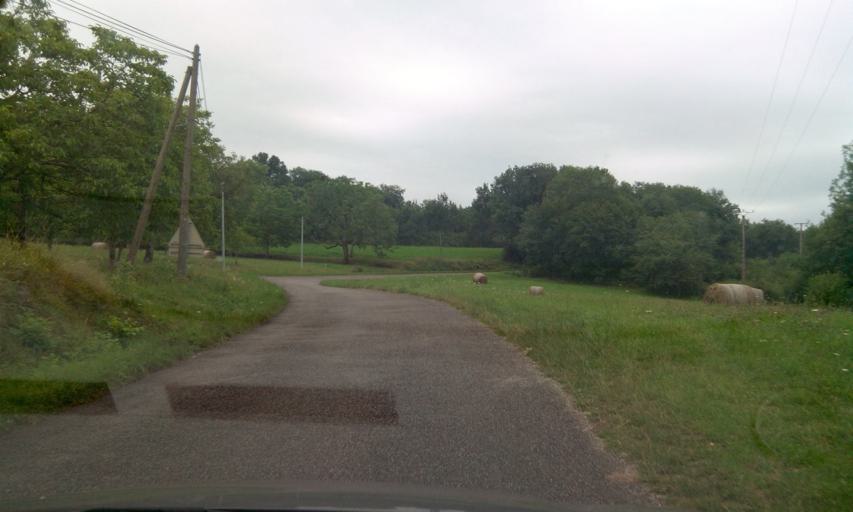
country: FR
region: Midi-Pyrenees
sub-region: Departement du Lot
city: Vayrac
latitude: 44.8941
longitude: 1.7518
